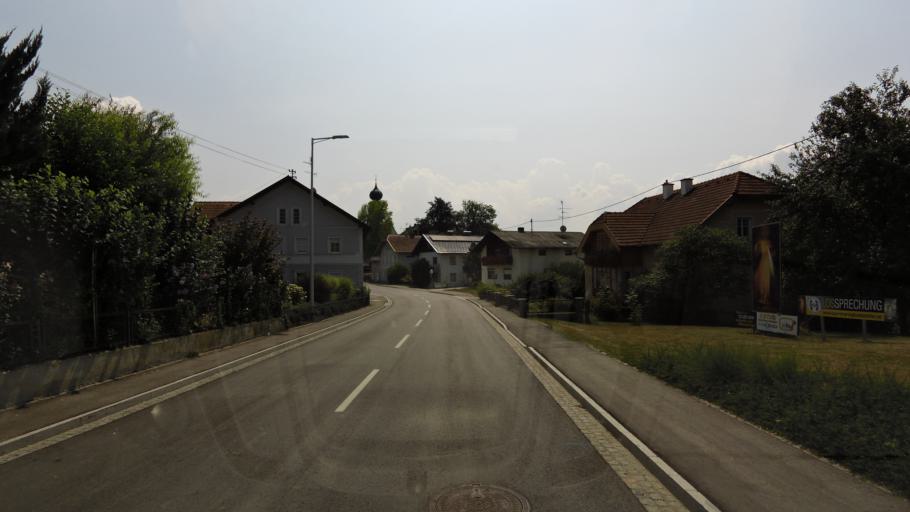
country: AT
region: Upper Austria
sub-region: Politischer Bezirk Braunau am Inn
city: Altheim
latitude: 48.2422
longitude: 13.3421
